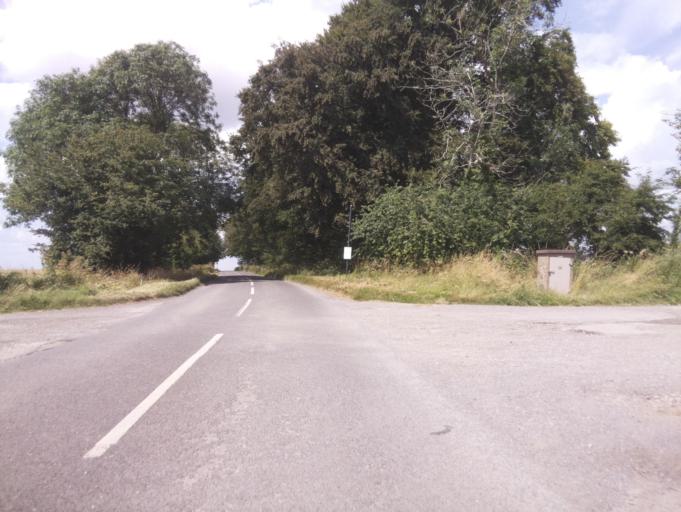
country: GB
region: England
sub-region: Borough of Swindon
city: Bishopstone
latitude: 51.5574
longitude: -1.6072
